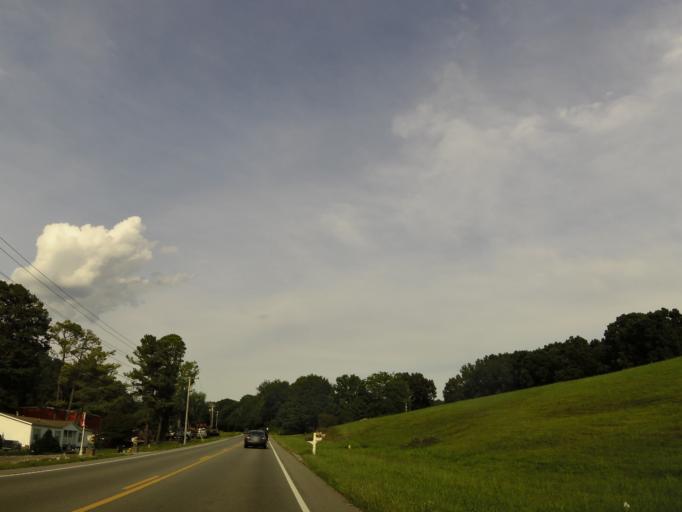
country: US
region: Tennessee
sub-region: Humphreys County
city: McEwen
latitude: 36.1026
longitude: -87.6653
